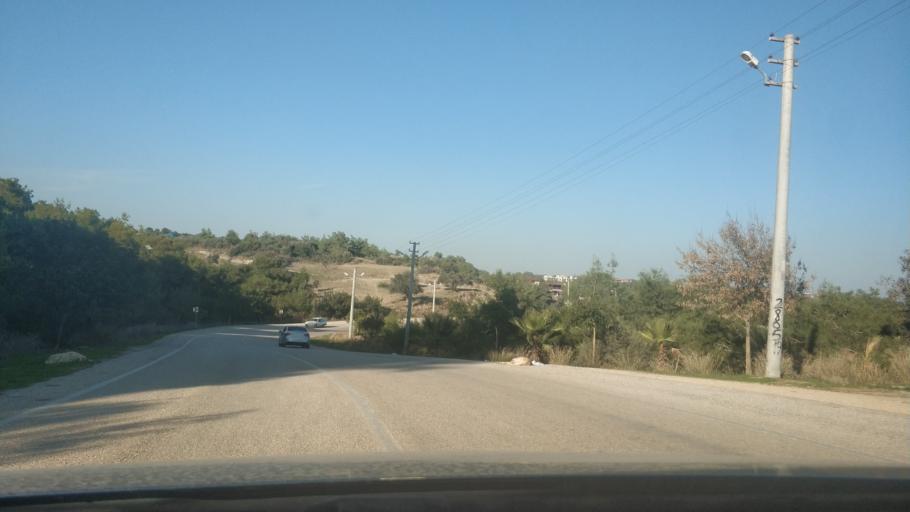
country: TR
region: Adana
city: Adana
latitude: 37.1003
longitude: 35.2907
